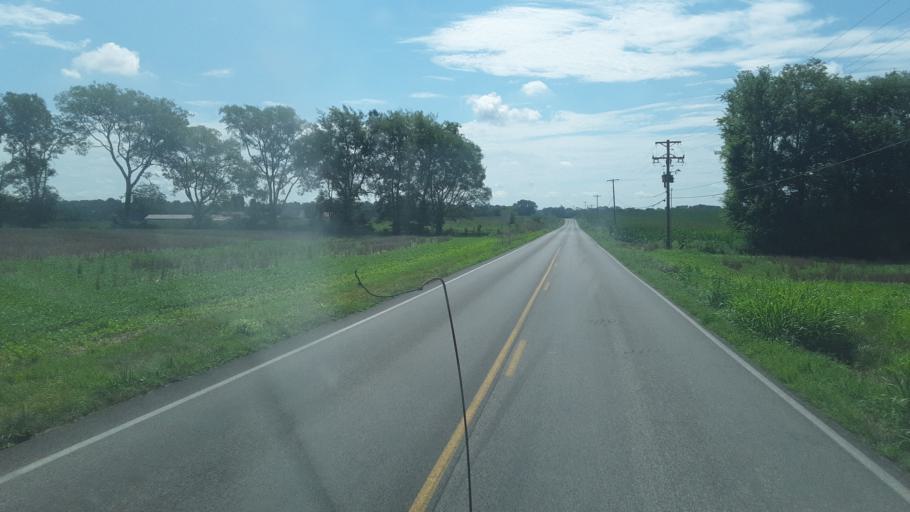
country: US
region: Kentucky
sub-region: Christian County
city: Oak Grove
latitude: 36.7734
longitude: -87.3430
